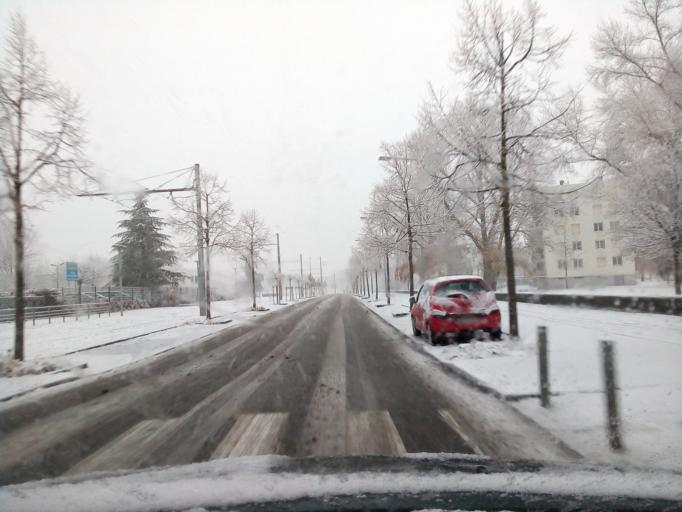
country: FR
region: Rhone-Alpes
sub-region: Departement de l'Isere
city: Saint-Martin-d'Heres
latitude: 45.1797
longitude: 5.7552
